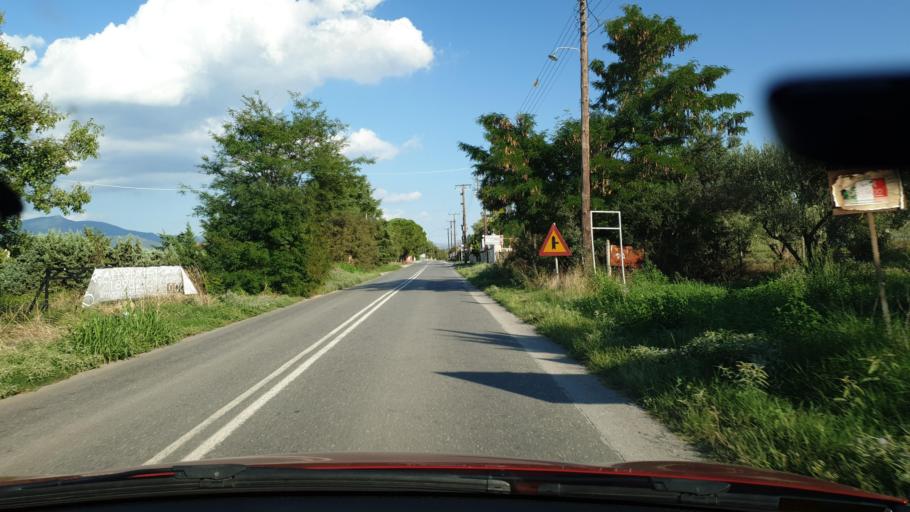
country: GR
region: Central Macedonia
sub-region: Nomos Thessalonikis
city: Souroti
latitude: 40.4795
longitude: 23.0717
